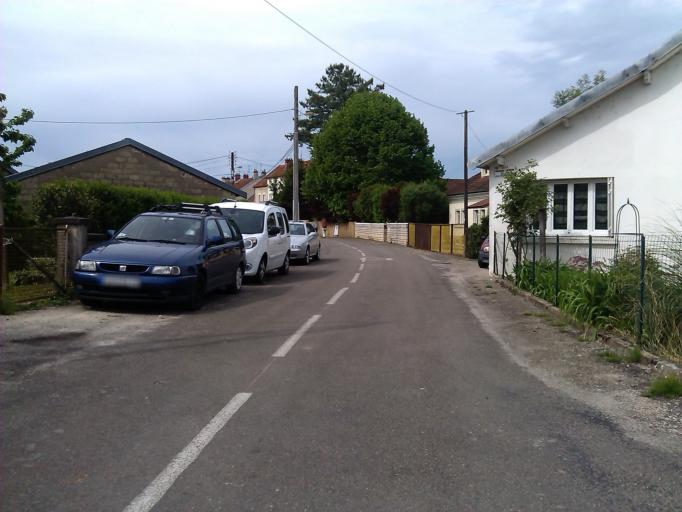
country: FR
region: Franche-Comte
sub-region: Departement du Jura
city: Dole
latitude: 47.1016
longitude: 5.4980
